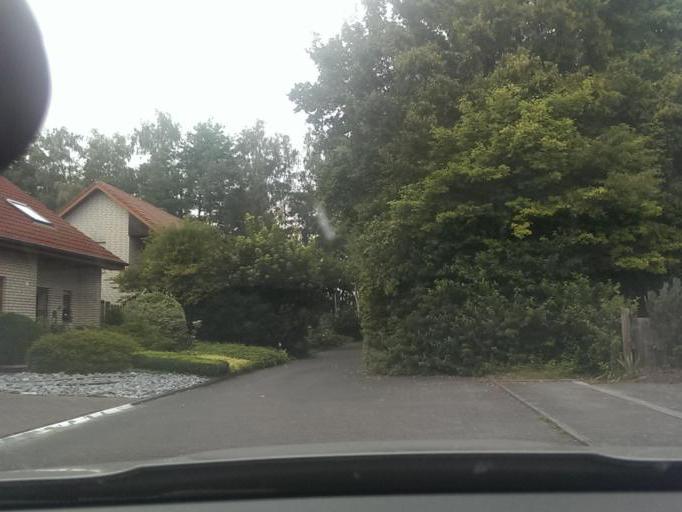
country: DE
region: North Rhine-Westphalia
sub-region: Regierungsbezirk Detmold
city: Delbruck
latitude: 51.7568
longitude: 8.5579
